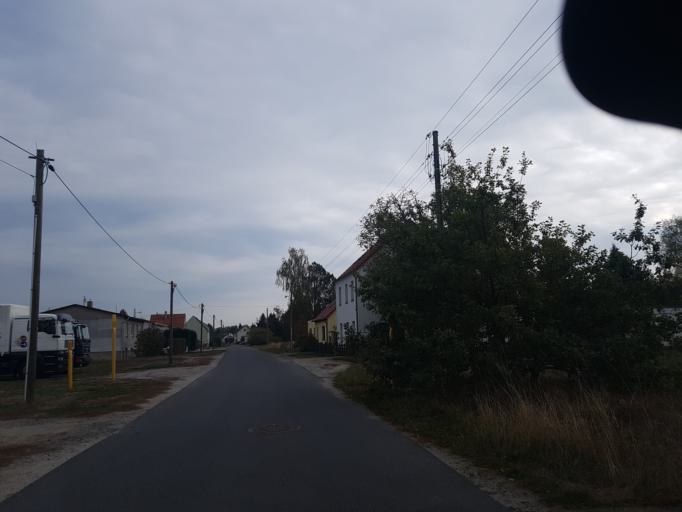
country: DE
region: Brandenburg
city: Finsterwalde
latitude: 51.6130
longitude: 13.7232
